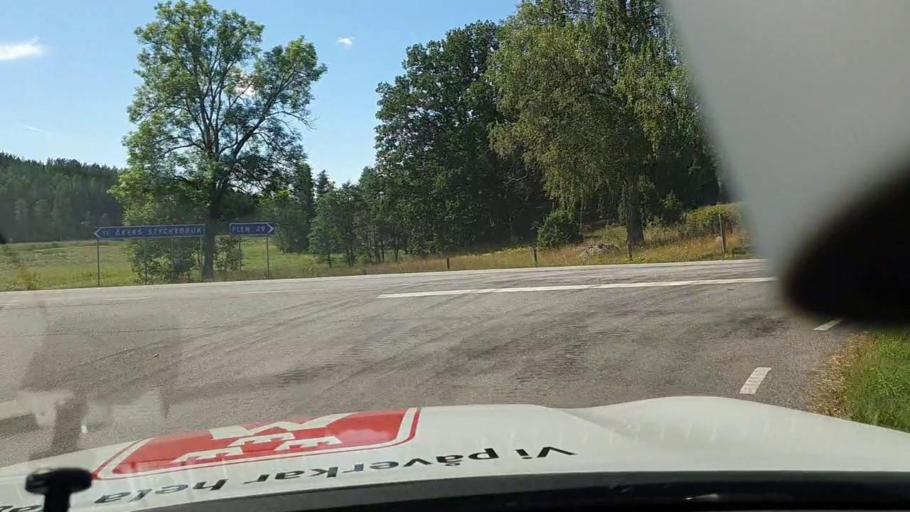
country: SE
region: Soedermanland
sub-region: Strangnas Kommun
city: Akers Styckebruk
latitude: 59.2699
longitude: 16.9808
